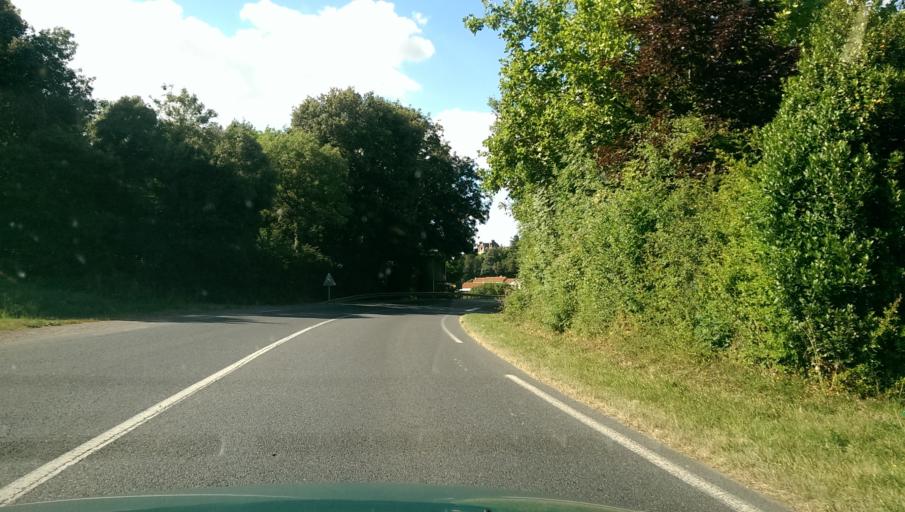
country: FR
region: Pays de la Loire
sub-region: Departement de la Vendee
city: Rocheserviere
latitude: 46.9336
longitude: -1.5137
